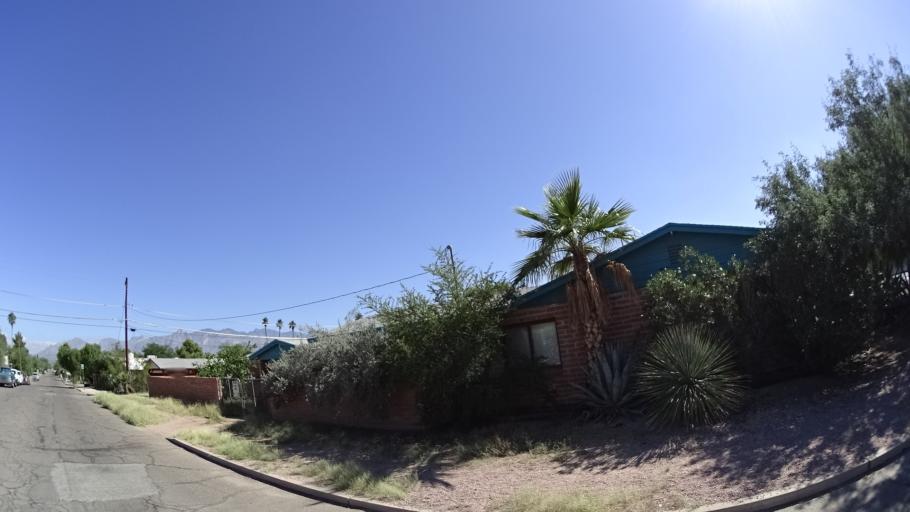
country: US
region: Arizona
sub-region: Pima County
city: Tucson
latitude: 32.2449
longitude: -110.9498
